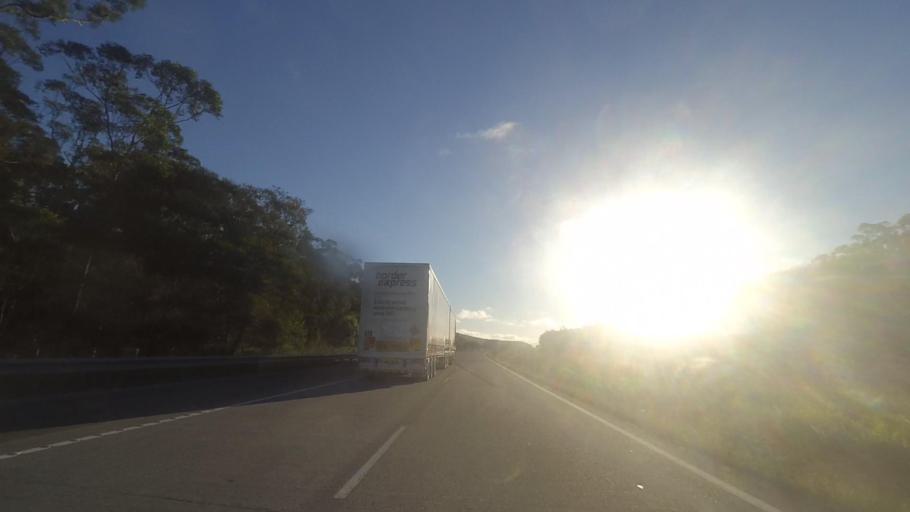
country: AU
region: New South Wales
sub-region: Great Lakes
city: Bulahdelah
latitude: -32.5193
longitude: 152.2054
